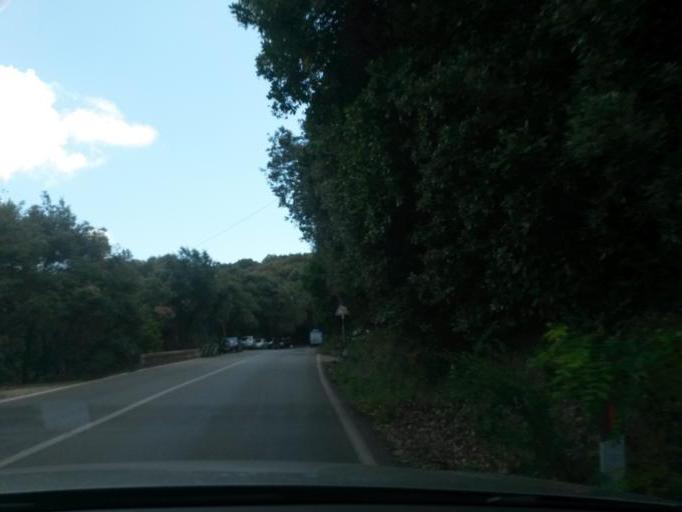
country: IT
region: Tuscany
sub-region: Provincia di Livorno
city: Marciana Marina
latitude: 42.7883
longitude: 10.2308
